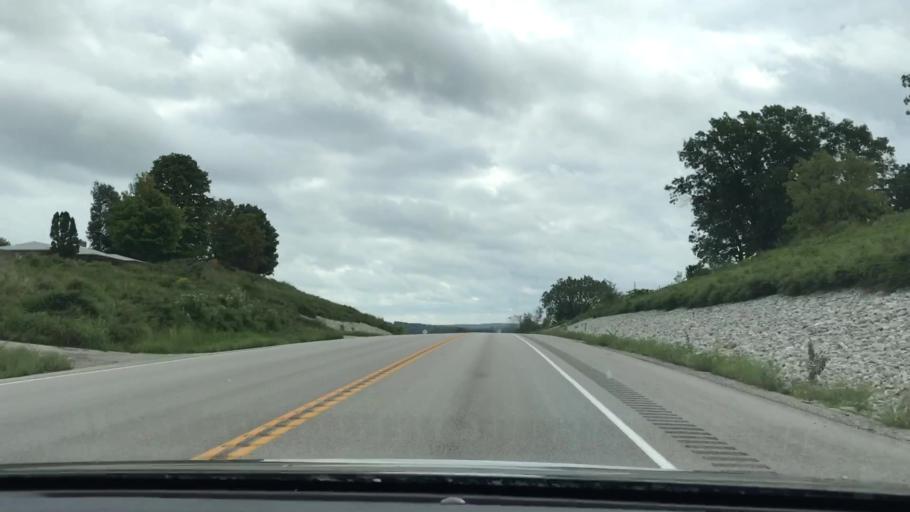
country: US
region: Kentucky
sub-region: Barren County
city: Glasgow
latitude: 36.9501
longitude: -85.8468
